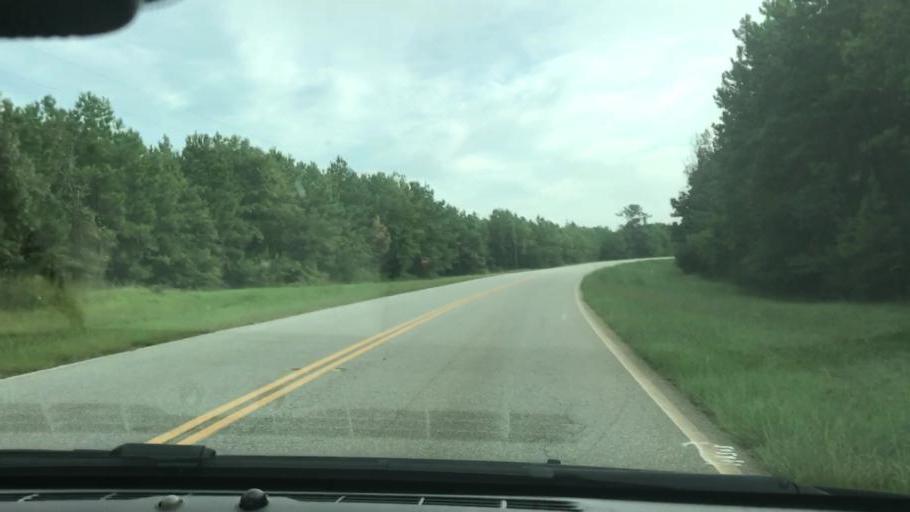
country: US
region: Georgia
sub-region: Stewart County
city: Lumpkin
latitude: 32.0159
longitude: -84.9306
